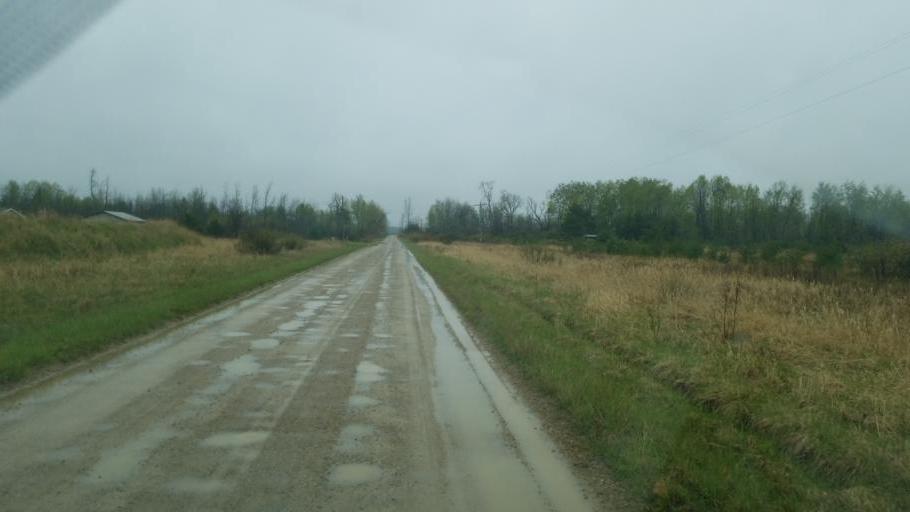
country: US
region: Michigan
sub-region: Montcalm County
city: Lakeview
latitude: 43.4956
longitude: -85.3186
